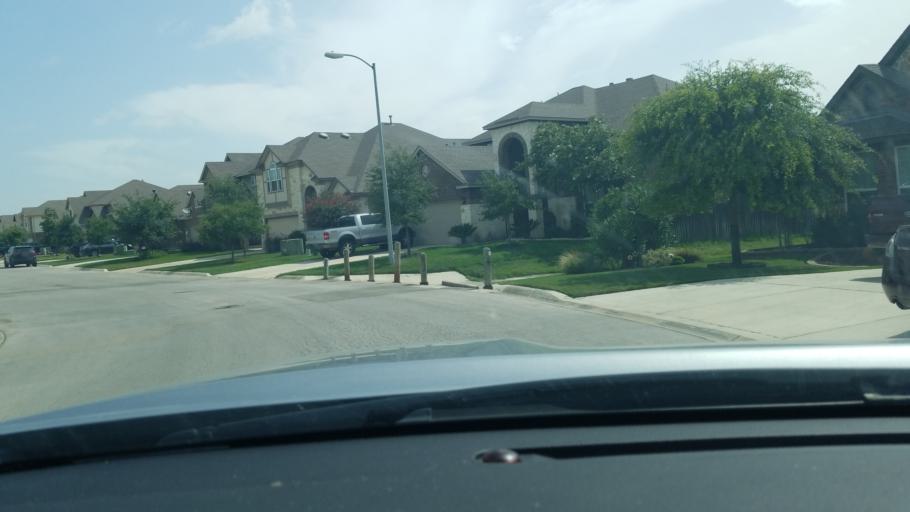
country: US
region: Texas
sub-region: Bexar County
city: Timberwood Park
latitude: 29.6906
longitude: -98.4921
